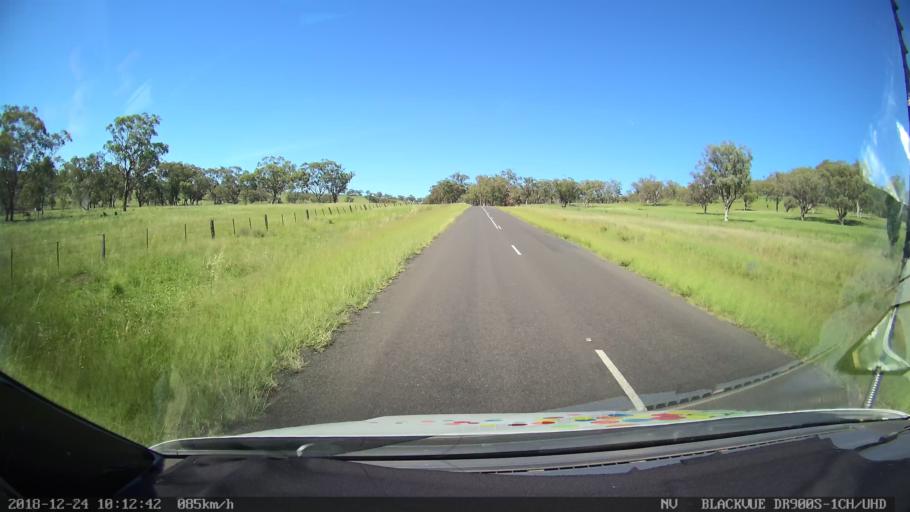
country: AU
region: New South Wales
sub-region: Liverpool Plains
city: Quirindi
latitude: -31.6818
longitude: 150.6454
